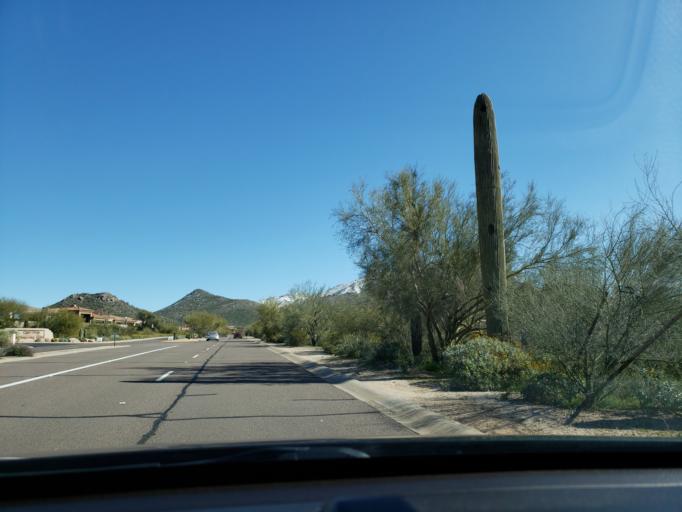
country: US
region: Arizona
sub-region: Maricopa County
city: Carefree
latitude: 33.7072
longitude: -111.8459
